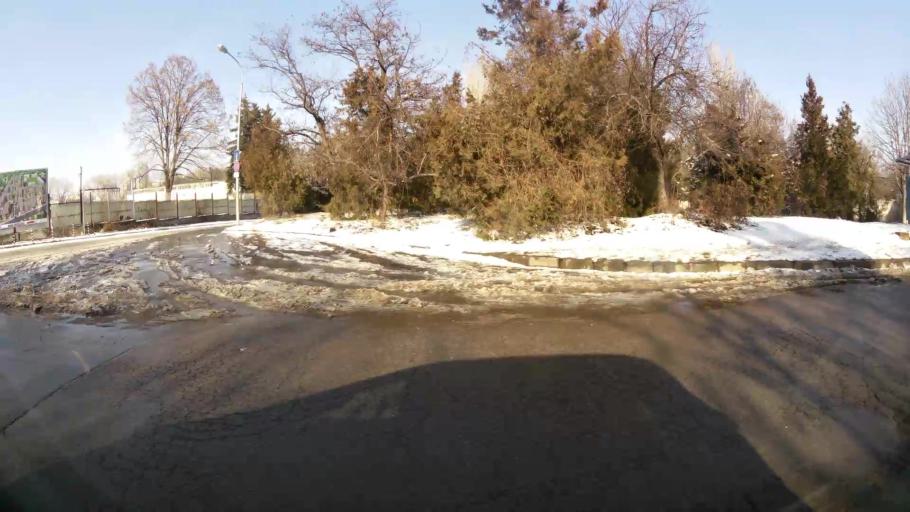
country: BG
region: Sofia-Capital
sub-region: Stolichna Obshtina
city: Sofia
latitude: 42.6591
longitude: 23.3273
